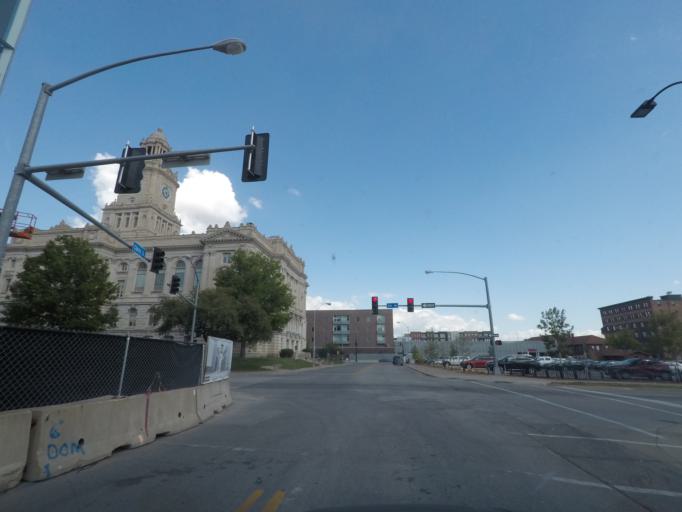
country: US
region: Iowa
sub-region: Polk County
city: Des Moines
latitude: 41.5840
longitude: -93.6241
